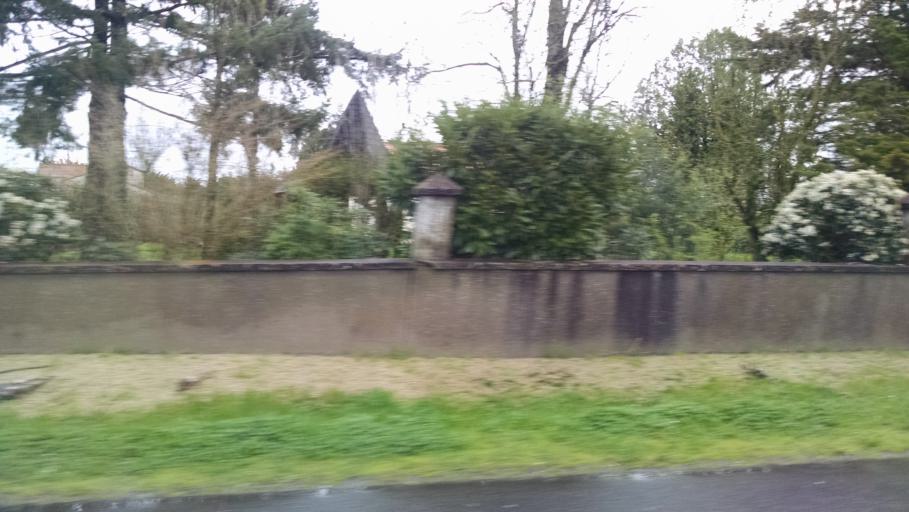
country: FR
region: Pays de la Loire
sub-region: Departement de la Loire-Atlantique
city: Aigrefeuille-sur-Maine
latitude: 47.0818
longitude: -1.4034
